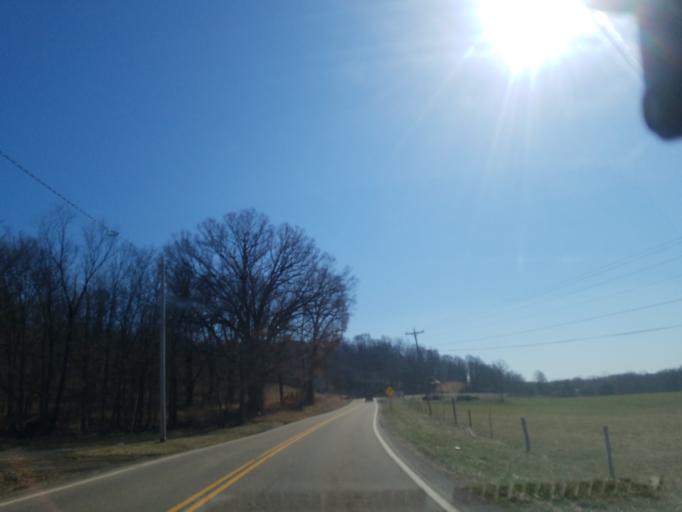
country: US
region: Ohio
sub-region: Tuscarawas County
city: Rockford
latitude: 40.5116
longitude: -81.2609
